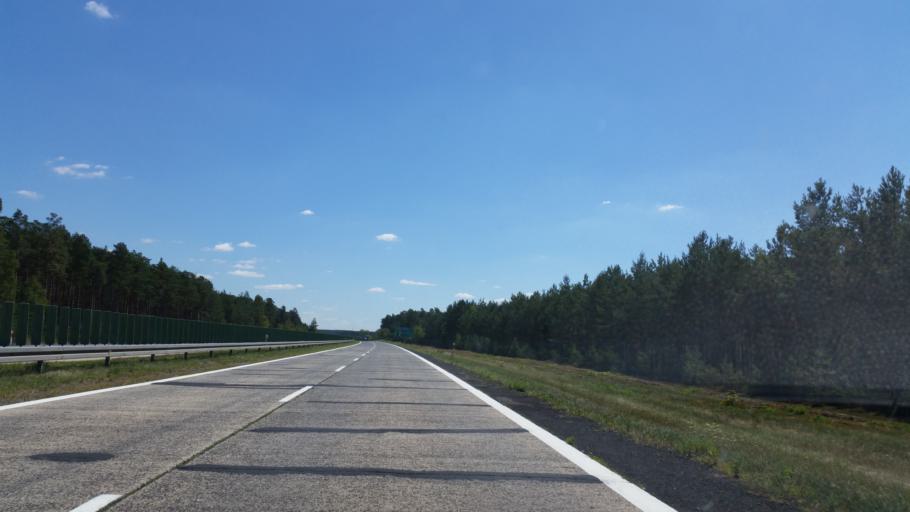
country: PL
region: Lower Silesian Voivodeship
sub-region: Powiat boleslawiecki
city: Boleslawiec
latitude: 51.3688
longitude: 15.5684
